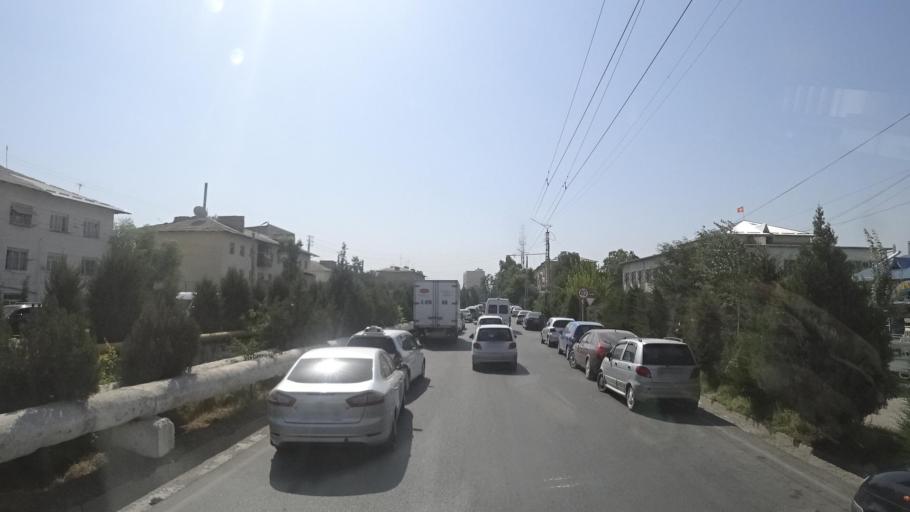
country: KG
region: Osh
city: Osh
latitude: 40.5201
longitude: 72.8095
